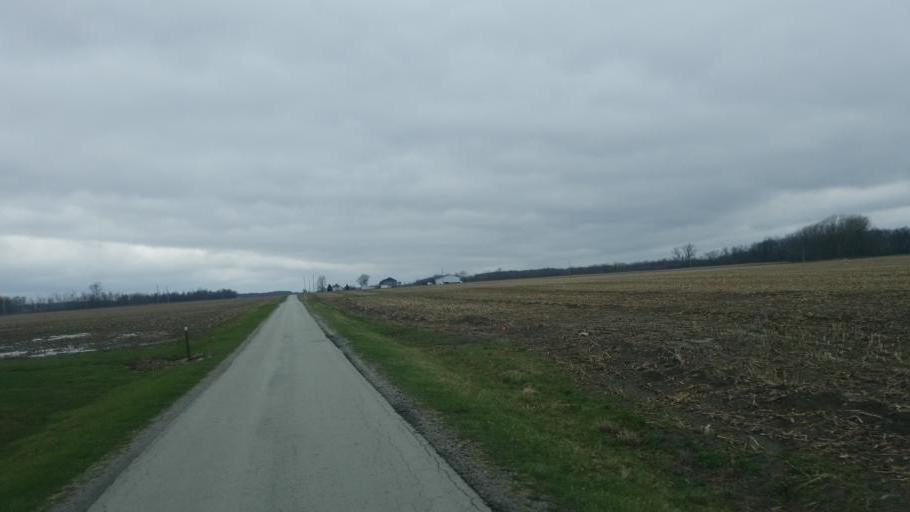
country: US
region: Ohio
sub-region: Hardin County
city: Forest
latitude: 40.7236
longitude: -83.4730
